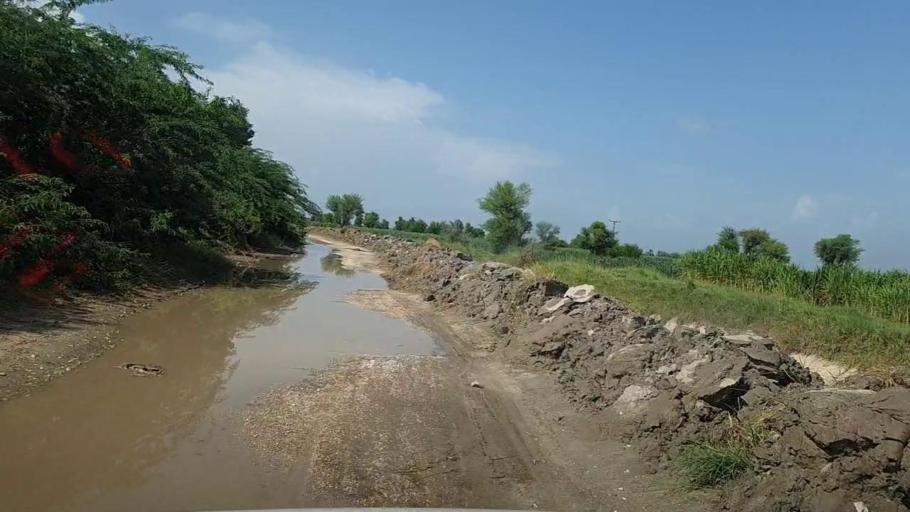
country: PK
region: Sindh
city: Bhiria
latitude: 26.8864
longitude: 68.2368
